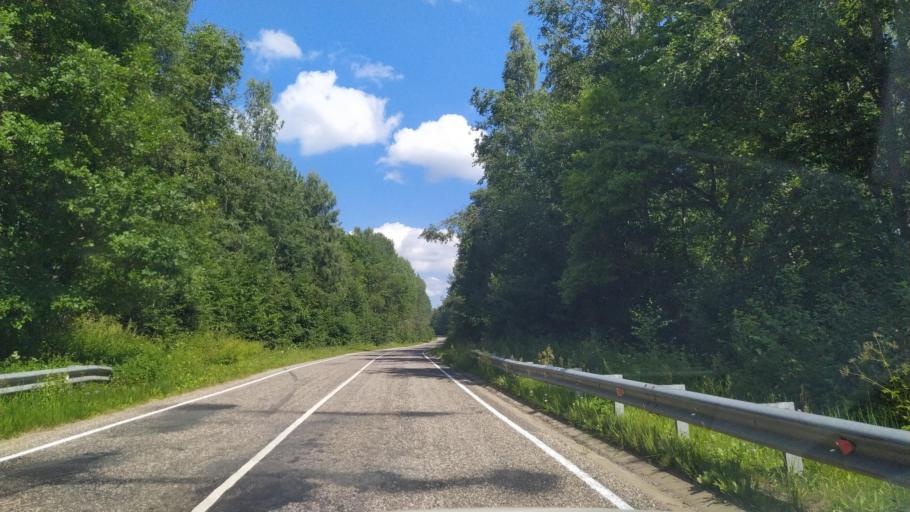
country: RU
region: Pskov
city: Pushkinskiye Gory
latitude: 57.0639
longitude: 28.9498
